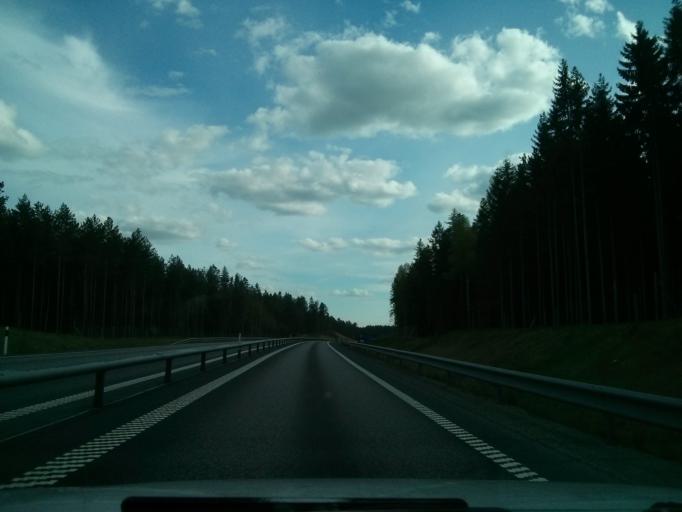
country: SE
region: Soedermanland
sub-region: Katrineholms Kommun
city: Katrineholm
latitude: 58.9778
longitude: 16.2657
